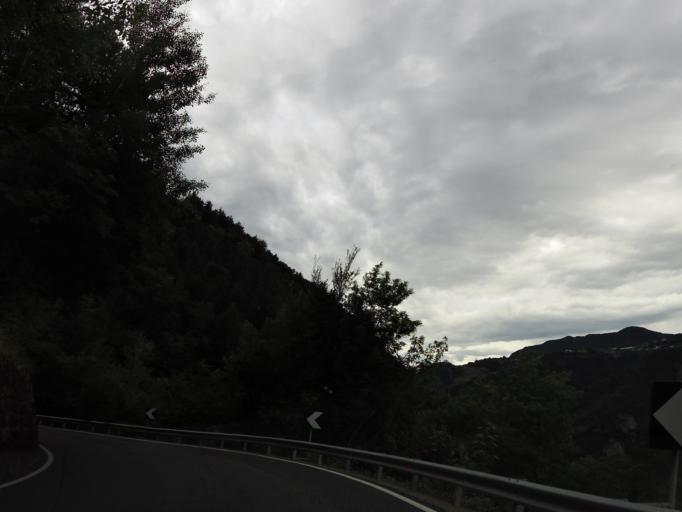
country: IT
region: Trentino-Alto Adige
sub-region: Bolzano
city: Fie Allo Sciliar
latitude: 46.5093
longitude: 11.4818
